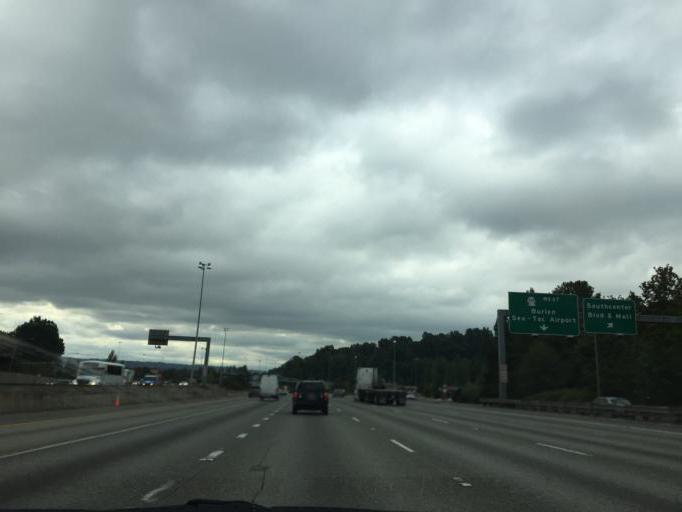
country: US
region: Washington
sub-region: King County
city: Tukwila
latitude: 47.4682
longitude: -122.2680
